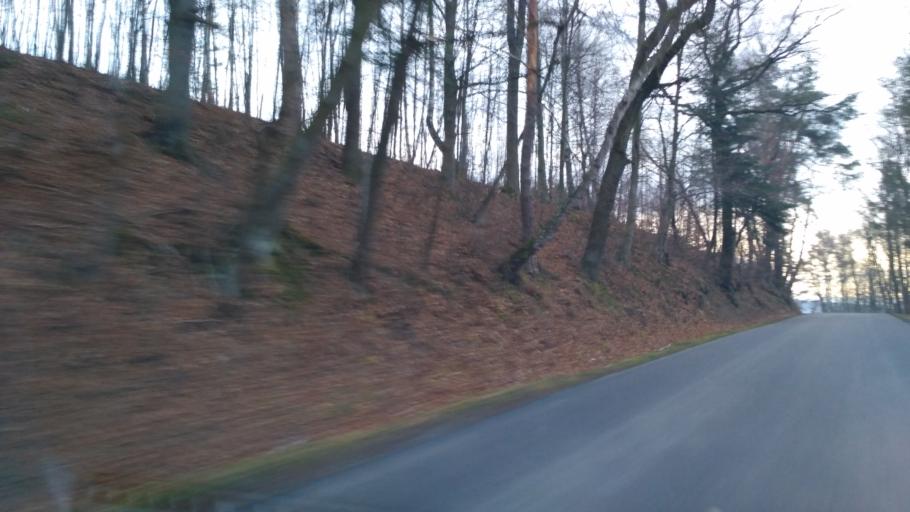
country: PL
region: Subcarpathian Voivodeship
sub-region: Powiat strzyzowski
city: Niebylec
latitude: 49.8585
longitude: 21.8961
